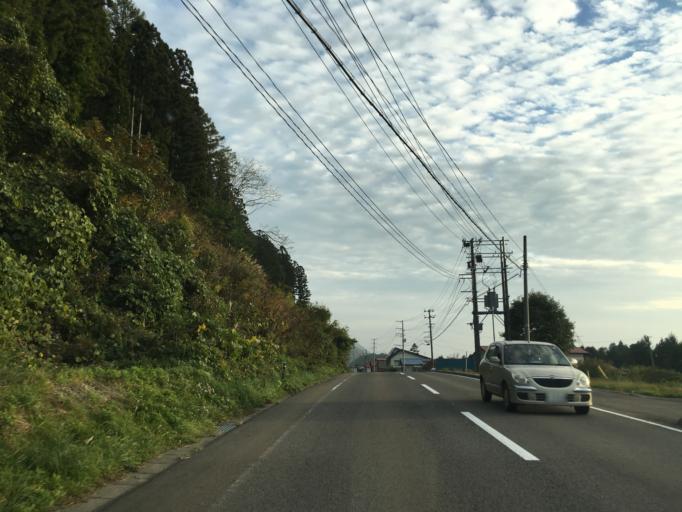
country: JP
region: Fukushima
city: Inawashiro
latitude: 37.5178
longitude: 140.1439
